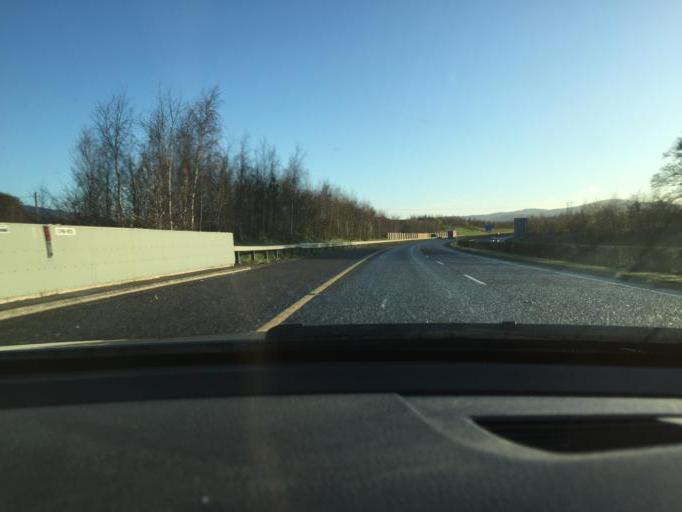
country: IE
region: Leinster
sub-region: Lu
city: Dundalk
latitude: 54.0299
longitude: -6.4325
